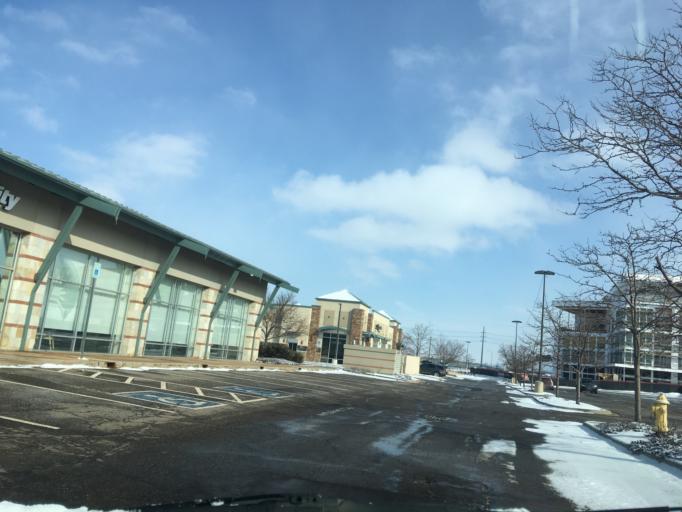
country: US
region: Colorado
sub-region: Broomfield County
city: Broomfield
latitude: 39.9307
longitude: -105.1242
